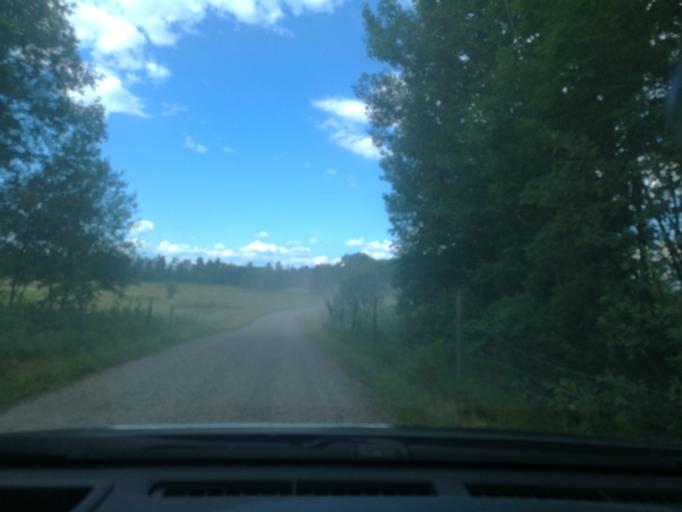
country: SE
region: Soedermanland
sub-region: Strangnas Kommun
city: Strangnas
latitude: 59.3970
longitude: 16.9662
